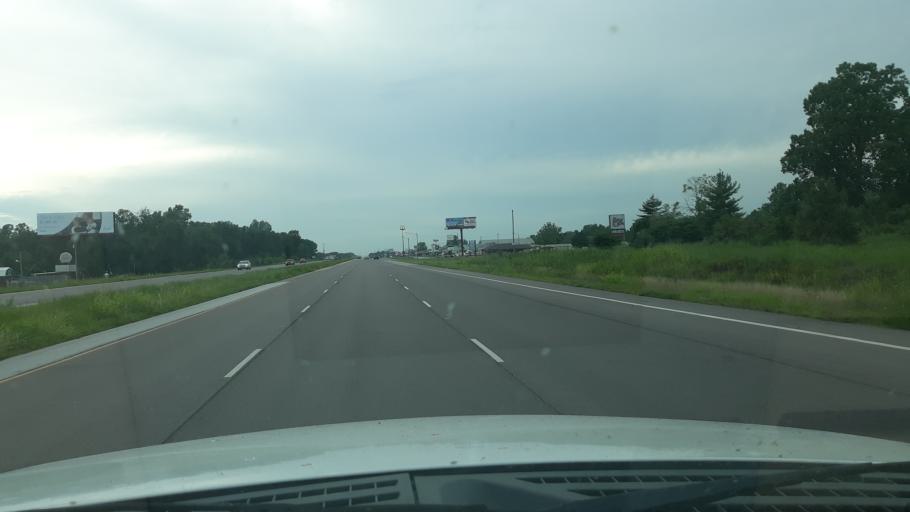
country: US
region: Illinois
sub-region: Williamson County
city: Crainville
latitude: 37.7452
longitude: -89.0649
